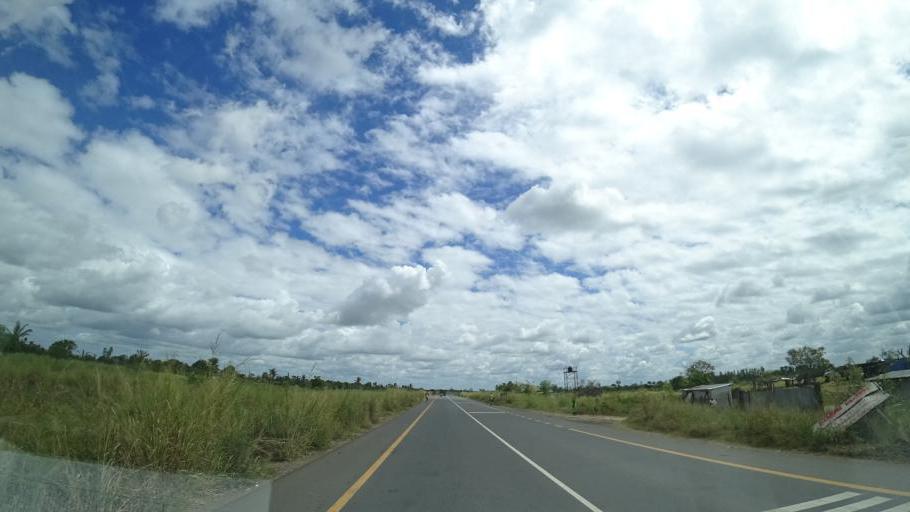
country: MZ
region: Sofala
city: Dondo
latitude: -19.3969
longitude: 34.4257
